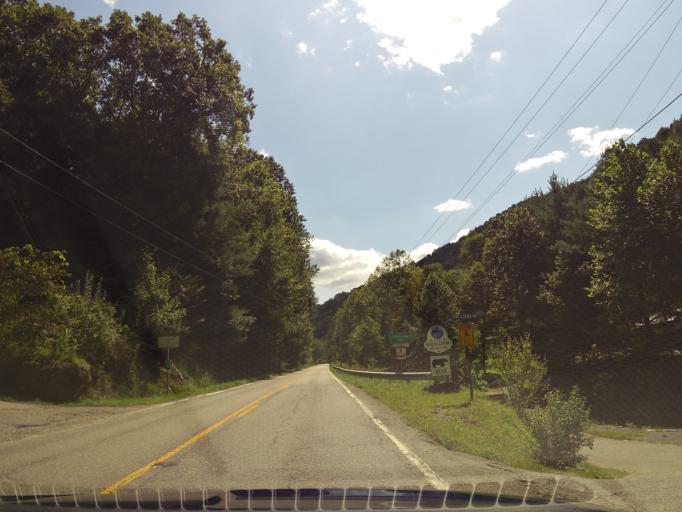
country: US
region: Kentucky
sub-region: Harlan County
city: Loyall
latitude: 36.9292
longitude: -83.3720
